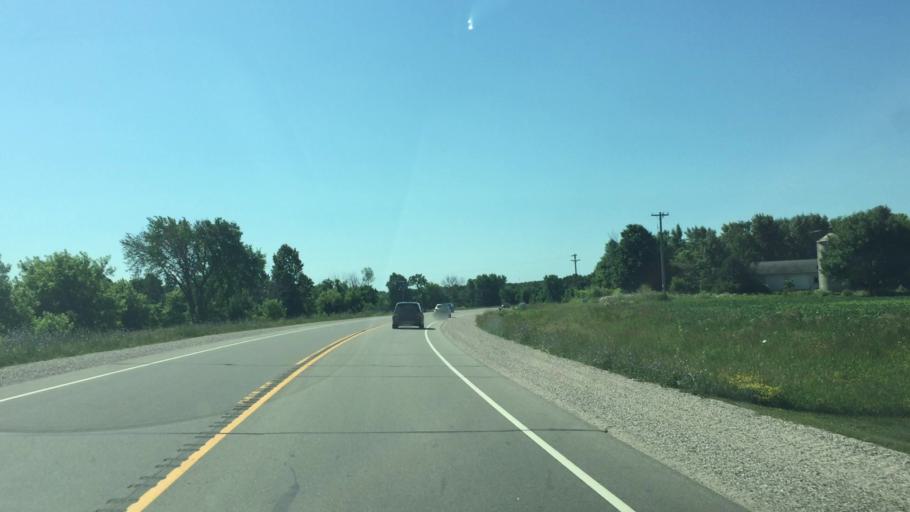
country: US
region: Wisconsin
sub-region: Calumet County
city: New Holstein
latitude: 43.9810
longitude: -88.1140
